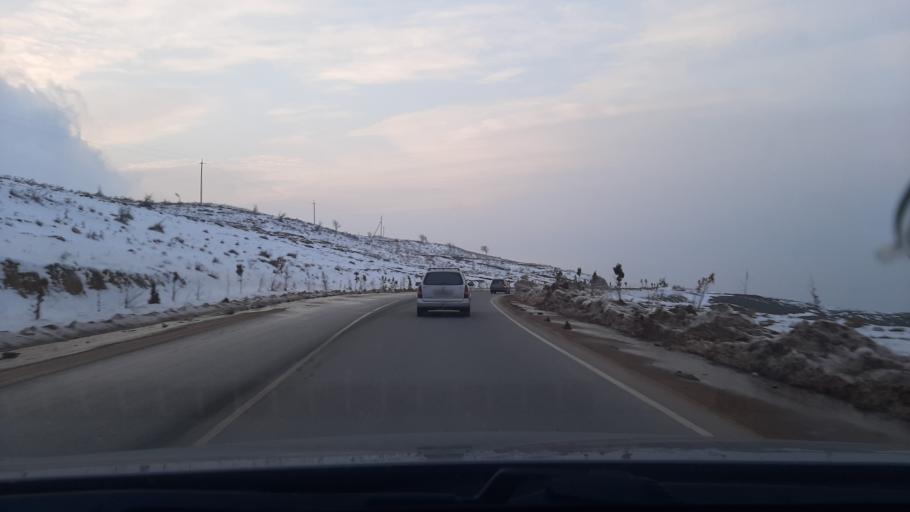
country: TJ
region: Republican Subordination
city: Vahdat
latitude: 38.4888
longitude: 69.1617
